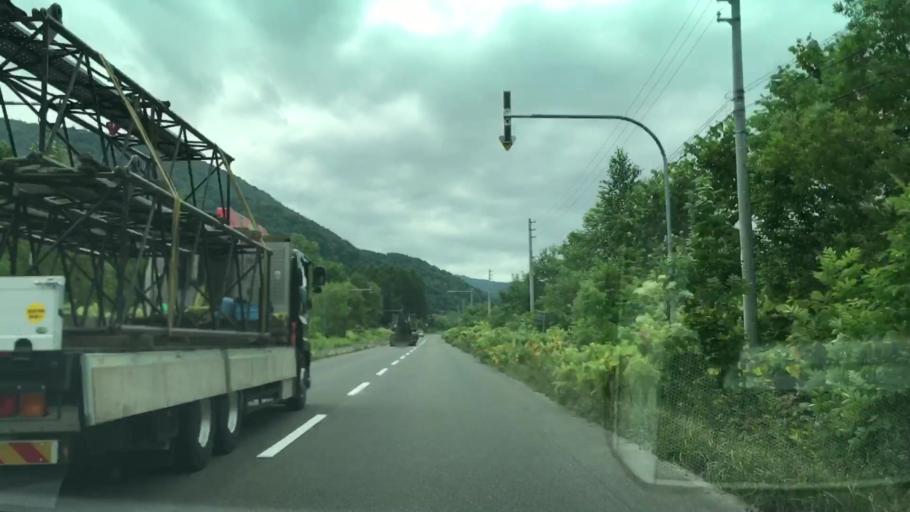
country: JP
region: Hokkaido
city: Yoichi
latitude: 43.0326
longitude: 140.8647
